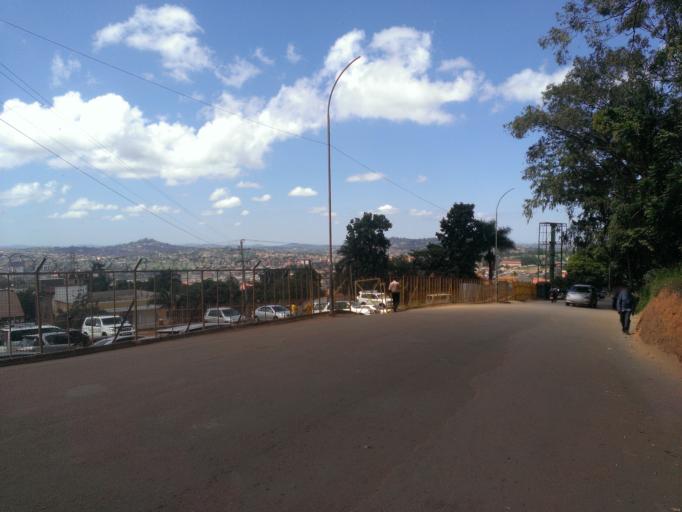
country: UG
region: Central Region
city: Kampala Central Division
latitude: 0.3152
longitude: 32.5608
